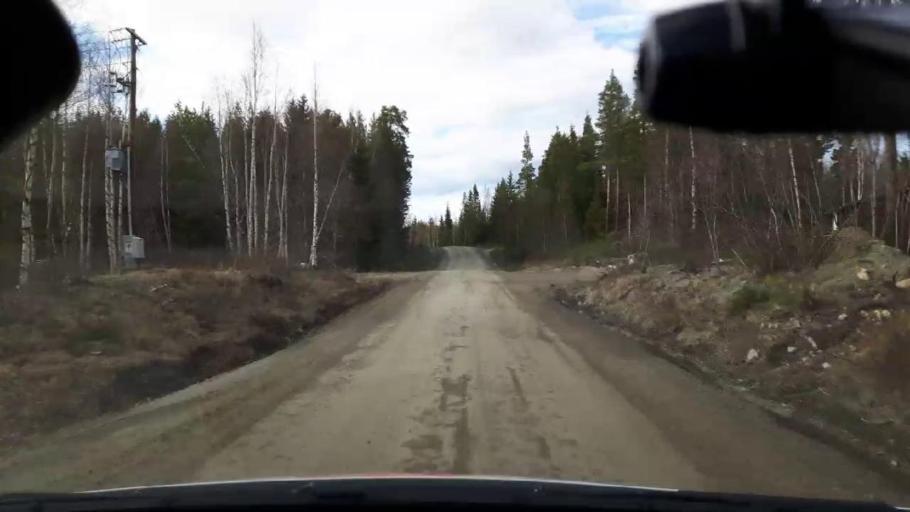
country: SE
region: Jaemtland
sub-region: Bergs Kommun
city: Hoverberg
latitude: 62.8905
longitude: 14.6570
